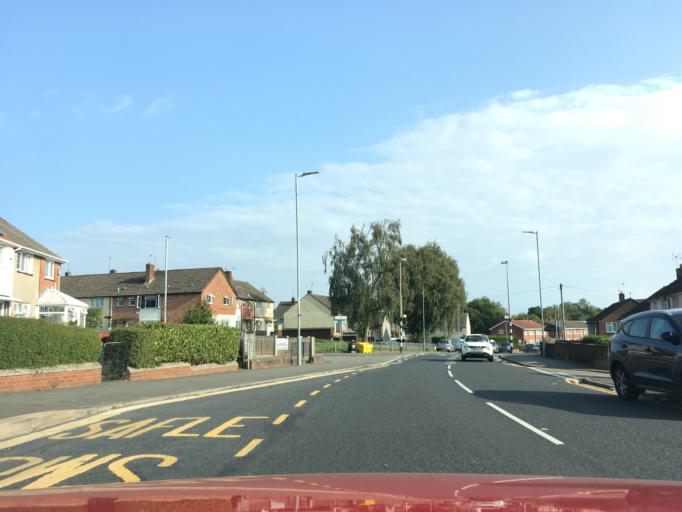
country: GB
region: Wales
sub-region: Newport
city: Newport
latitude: 51.6114
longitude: -3.0201
